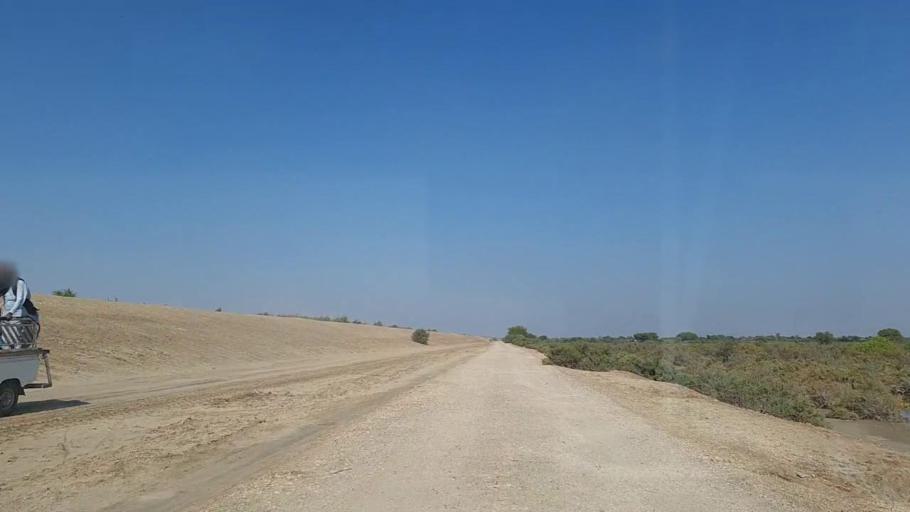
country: PK
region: Sindh
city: Chuhar Jamali
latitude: 24.4604
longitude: 68.0023
